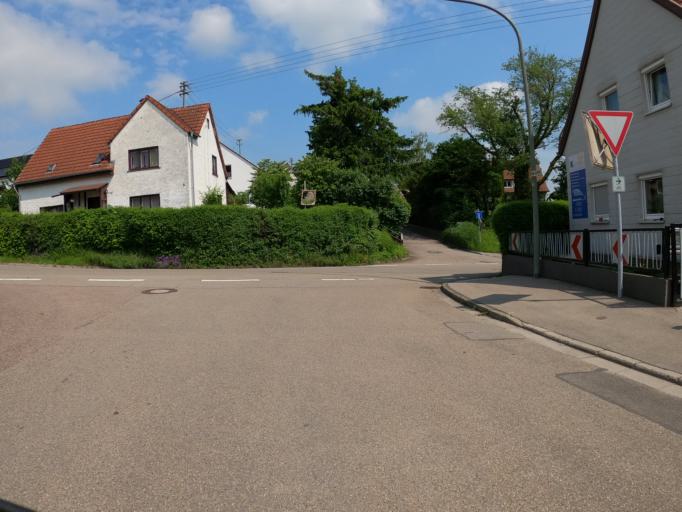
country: DE
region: Bavaria
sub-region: Swabia
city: Holzheim
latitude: 48.3788
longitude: 10.0965
